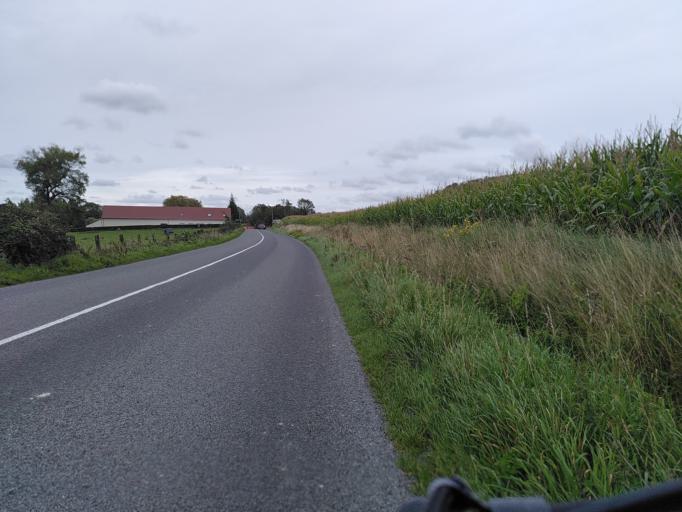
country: FR
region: Nord-Pas-de-Calais
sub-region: Departement du Pas-de-Calais
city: Desvres
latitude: 50.6699
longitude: 1.8558
